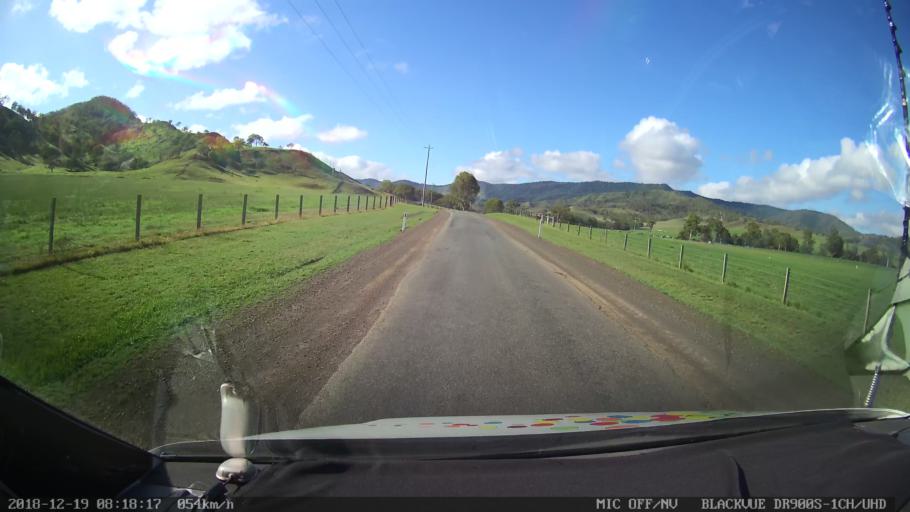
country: AU
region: New South Wales
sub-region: Kyogle
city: Kyogle
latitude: -28.2718
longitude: 152.9092
